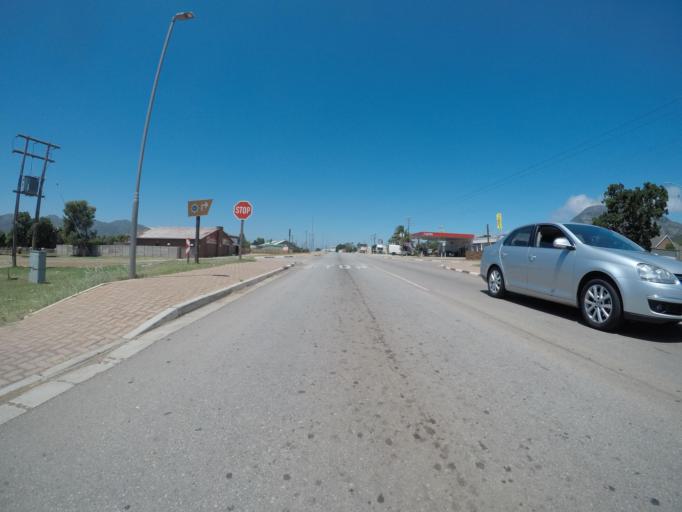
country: ZA
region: Eastern Cape
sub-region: Cacadu District Municipality
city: Kareedouw
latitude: -33.9523
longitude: 24.2940
